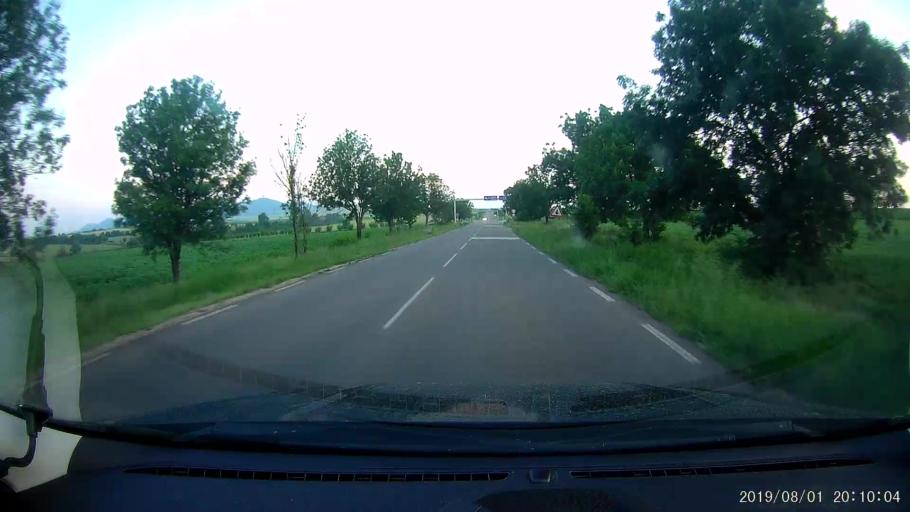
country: BG
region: Yambol
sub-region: Obshtina Yambol
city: Yambol
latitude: 42.4875
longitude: 26.5962
